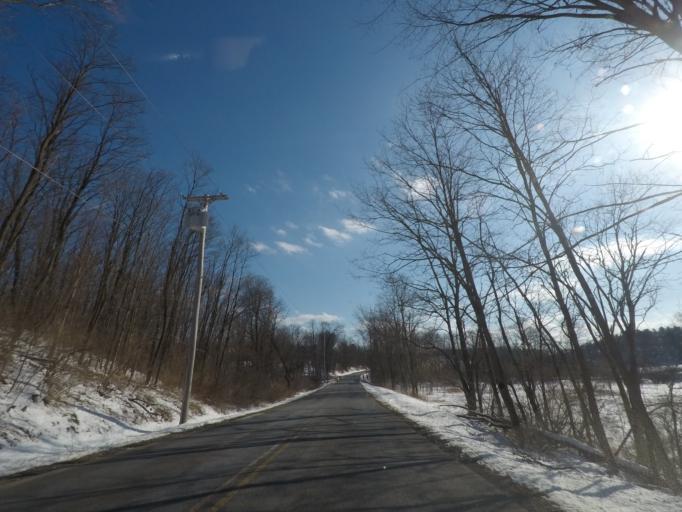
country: US
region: New York
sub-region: Rensselaer County
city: Hoosick Falls
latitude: 42.8802
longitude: -73.4988
